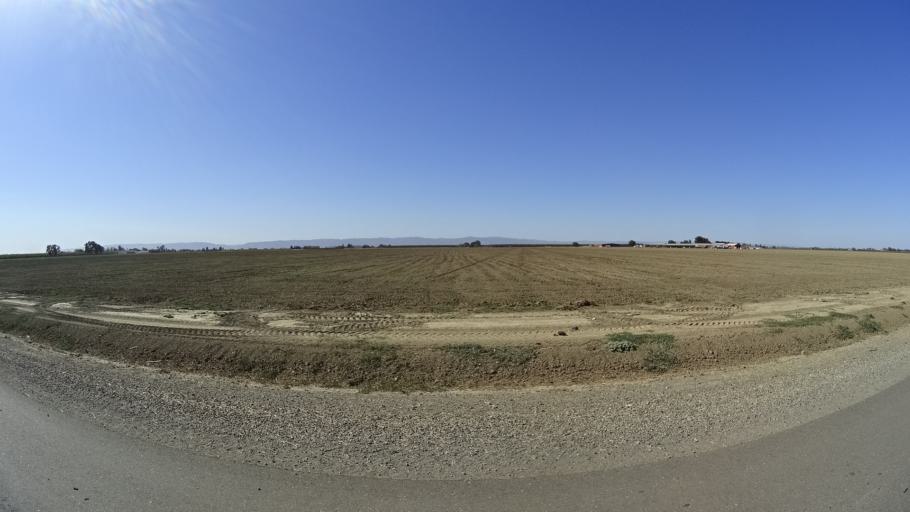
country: US
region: California
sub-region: Yolo County
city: Woodland
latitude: 38.6295
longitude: -121.8030
